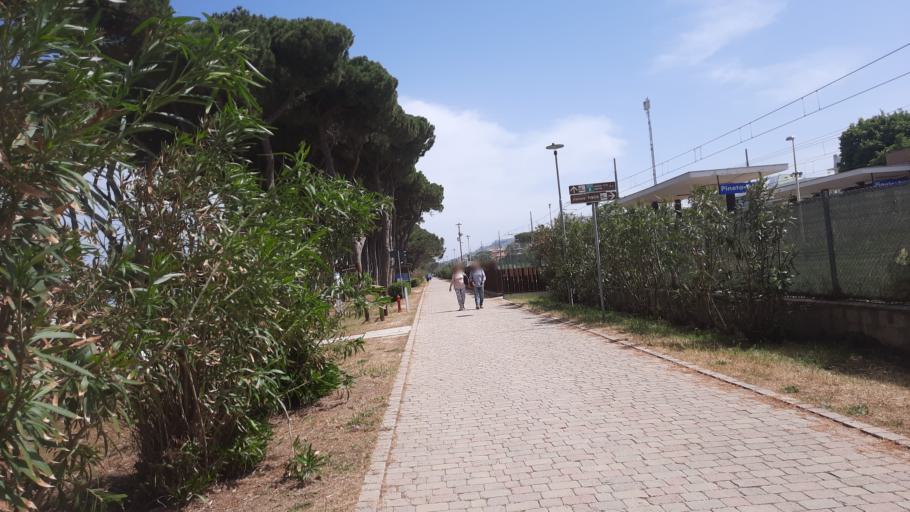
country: IT
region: Abruzzo
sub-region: Provincia di Teramo
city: Pineto
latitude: 42.6081
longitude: 14.0691
